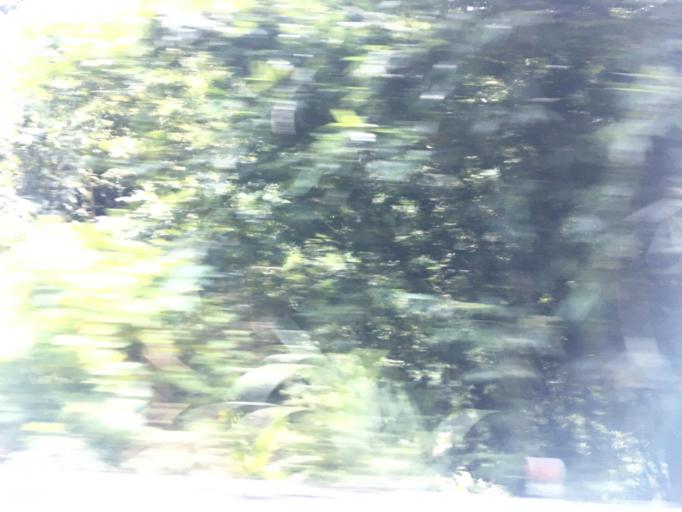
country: TW
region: Taiwan
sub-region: Yilan
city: Yilan
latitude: 24.8168
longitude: 121.7367
